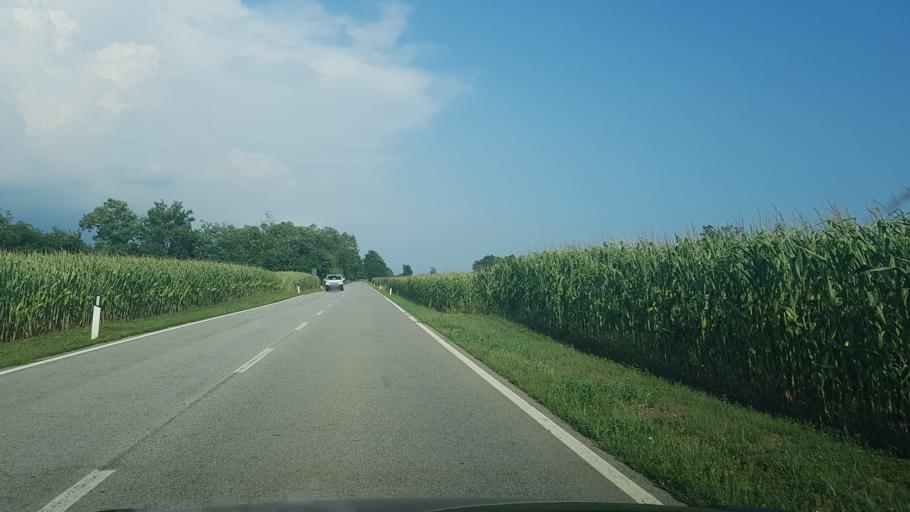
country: IT
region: Friuli Venezia Giulia
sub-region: Provincia di Udine
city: Basiliano-Vissandone
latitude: 46.0571
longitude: 13.1002
